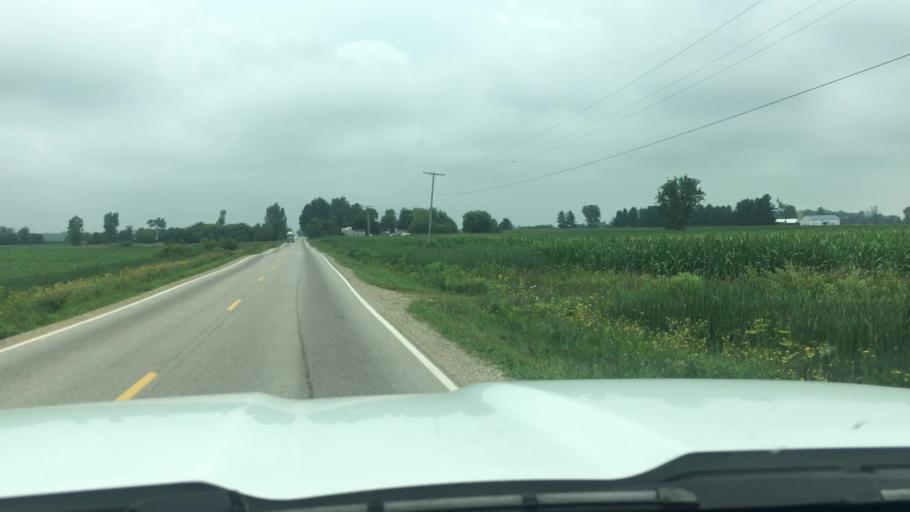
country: US
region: Michigan
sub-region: Sanilac County
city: Brown City
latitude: 43.2610
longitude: -82.9821
